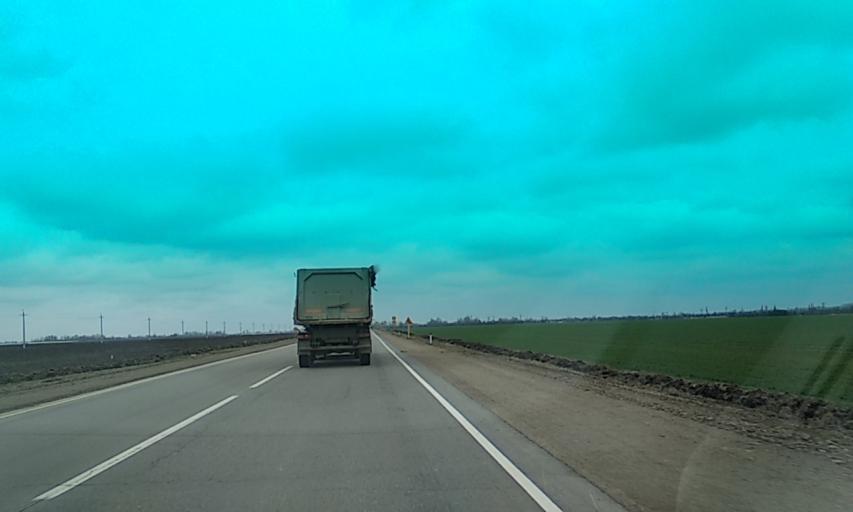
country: RU
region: Adygeya
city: Beloye
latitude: 45.0263
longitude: 39.6850
